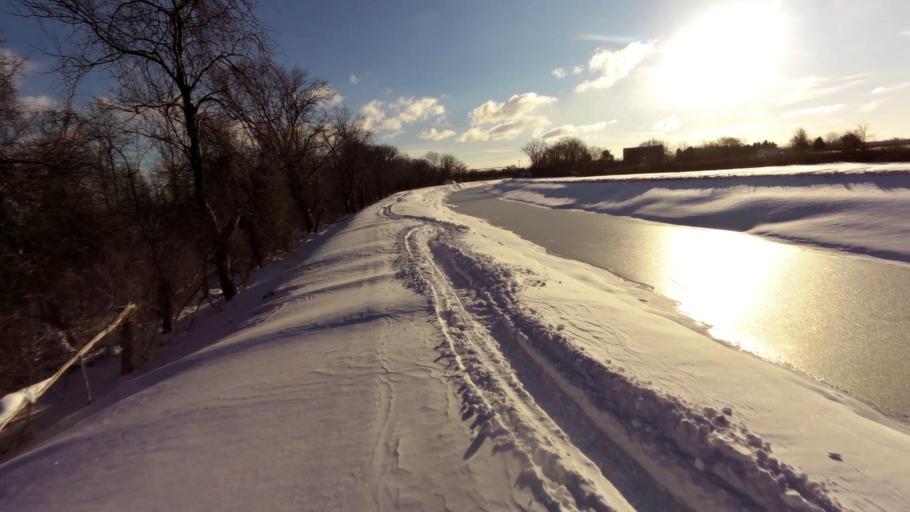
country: US
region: New York
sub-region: Orleans County
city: Albion
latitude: 43.2506
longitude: -78.2724
